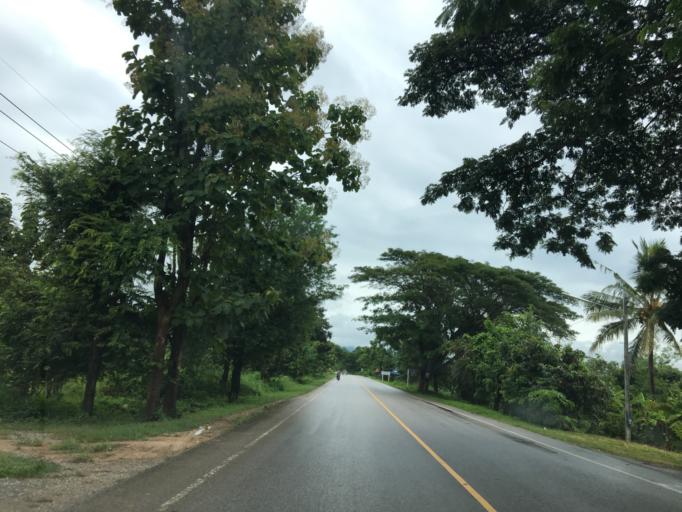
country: TH
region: Chiang Rai
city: Pa Daet
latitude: 19.4976
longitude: 99.9729
